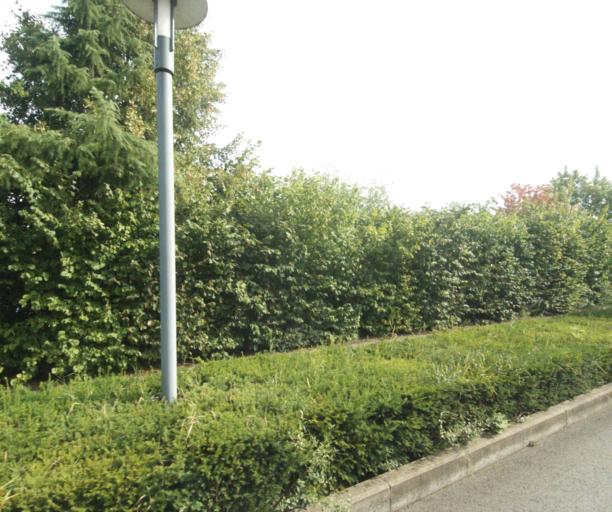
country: FR
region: Nord-Pas-de-Calais
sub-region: Departement du Nord
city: Lille
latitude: 50.6156
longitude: 3.0515
